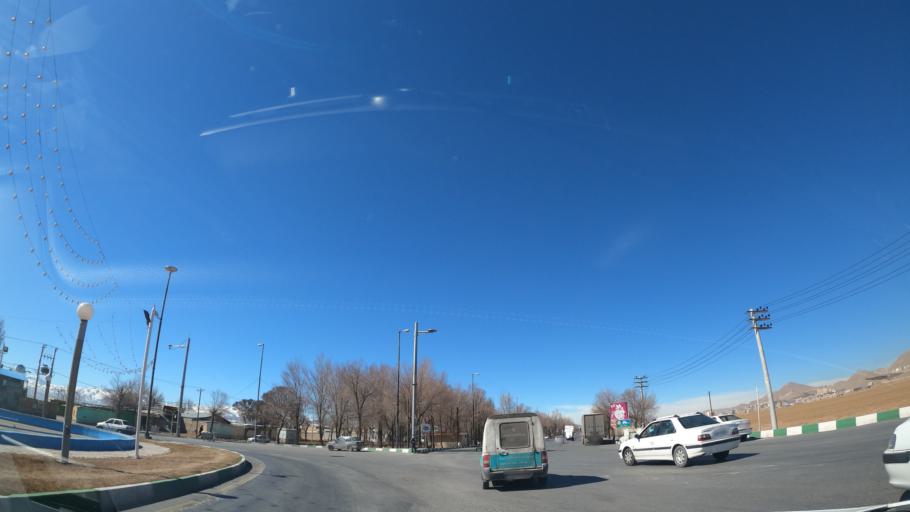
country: IR
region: Chahar Mahall va Bakhtiari
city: Shahrekord
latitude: 32.3078
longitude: 50.9015
